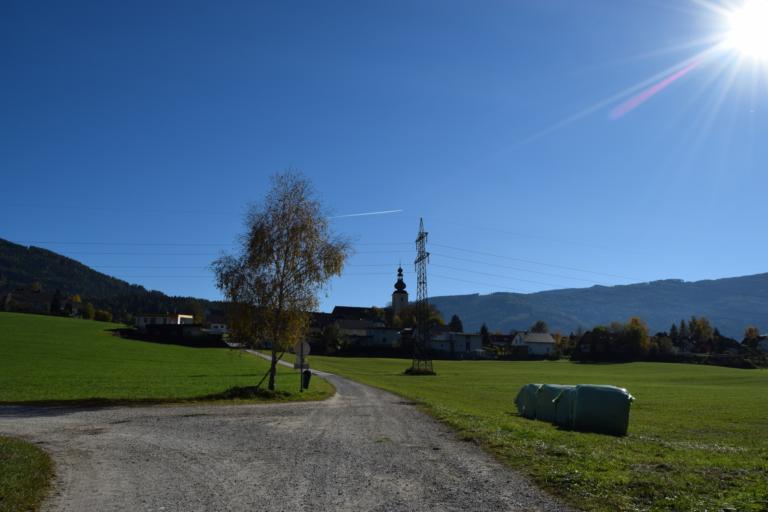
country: AT
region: Styria
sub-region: Politischer Bezirk Liezen
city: Irdning
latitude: 47.5095
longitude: 14.1045
